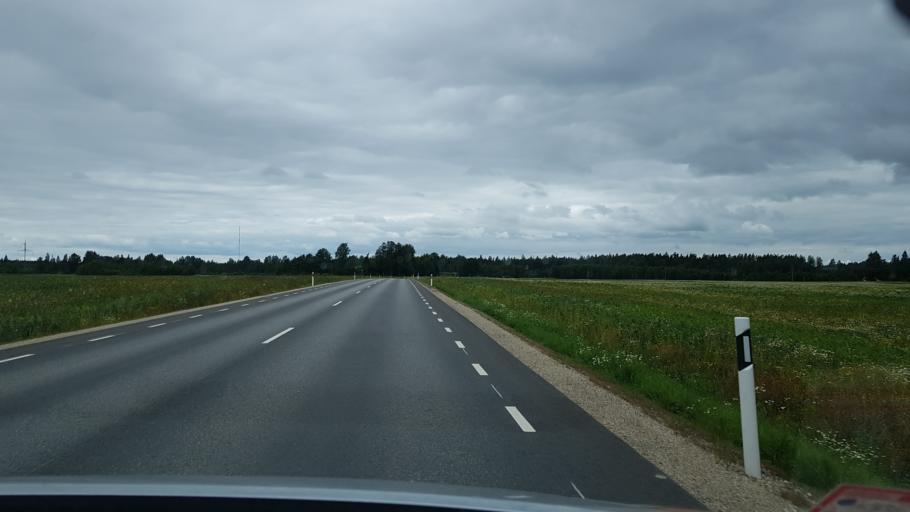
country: EE
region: Polvamaa
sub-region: Polva linn
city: Polva
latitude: 58.0774
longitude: 27.2475
